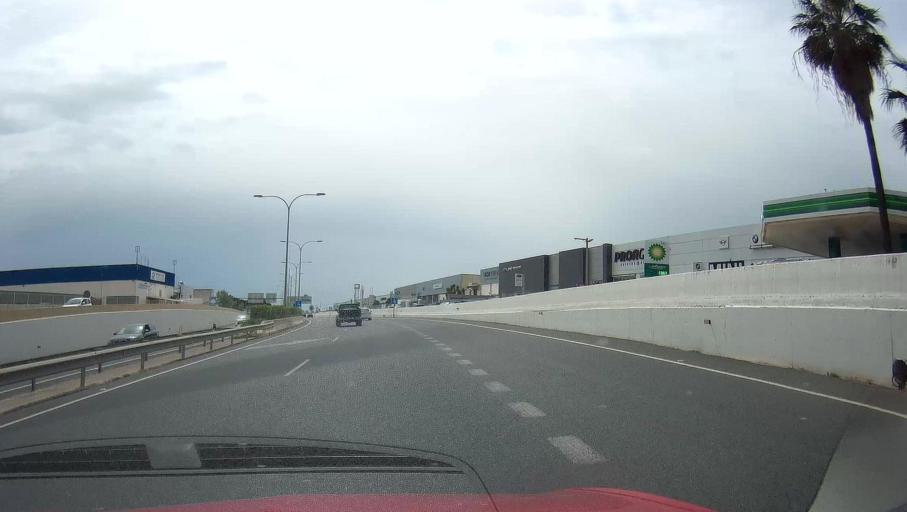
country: ES
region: Balearic Islands
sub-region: Illes Balears
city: Ibiza
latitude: 38.8859
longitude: 1.3925
